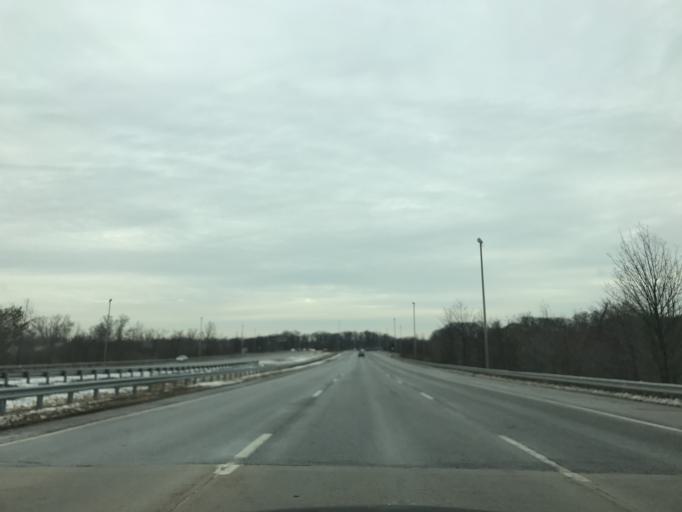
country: US
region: New Jersey
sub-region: Mercer County
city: White Horse
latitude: 40.1800
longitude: -74.7223
